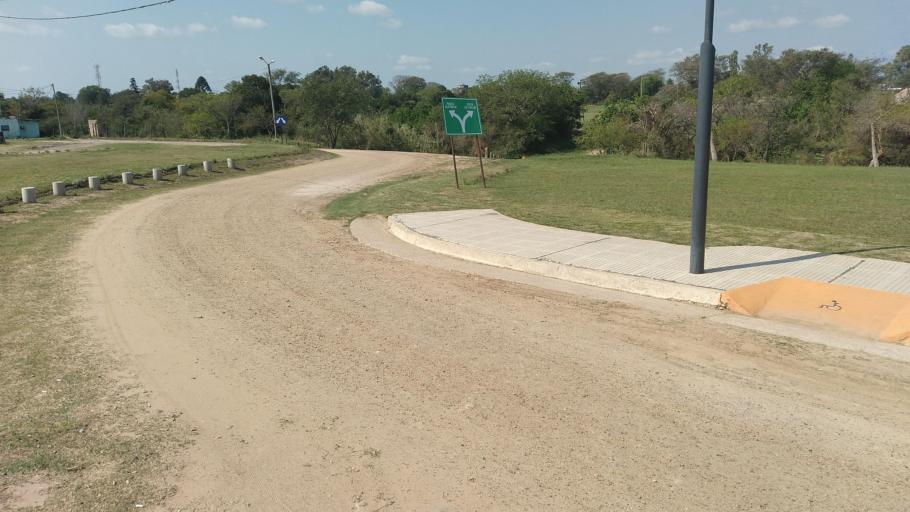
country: AR
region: Entre Rios
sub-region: Departamento de La Paz
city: La Paz
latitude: -30.7489
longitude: -59.6543
